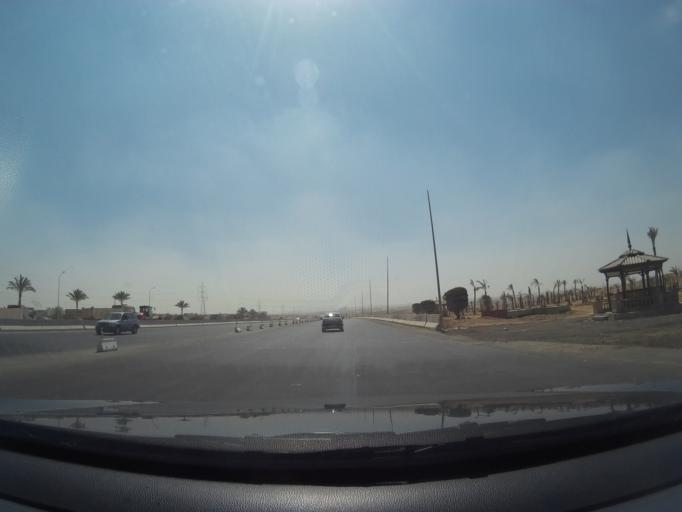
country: EG
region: As Suways
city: Ain Sukhna
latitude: 29.7632
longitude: 31.9614
